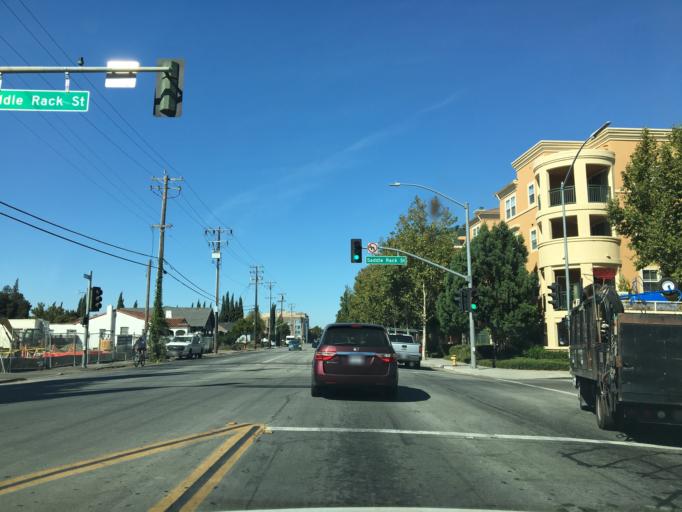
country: US
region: California
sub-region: Santa Clara County
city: Buena Vista
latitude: 37.3194
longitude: -121.9137
